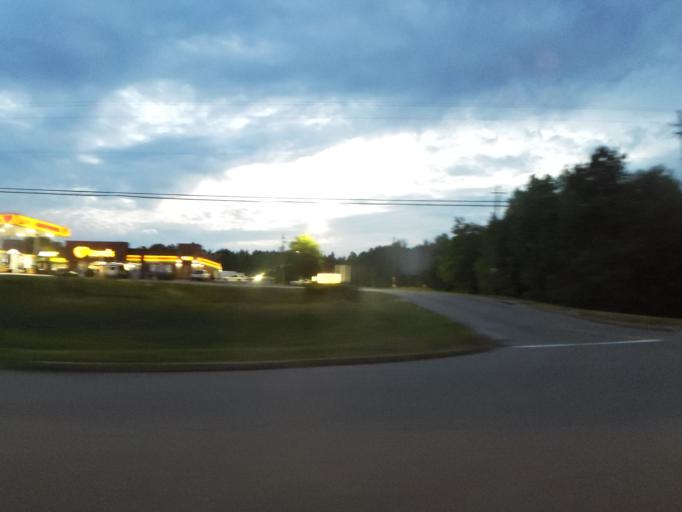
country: US
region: Georgia
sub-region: McDuffie County
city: Thomson
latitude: 33.5148
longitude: -82.5027
